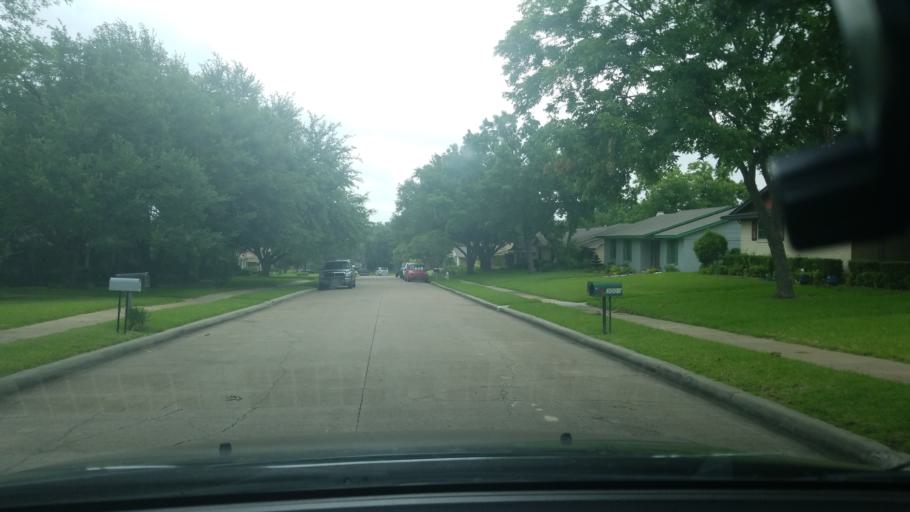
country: US
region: Texas
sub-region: Dallas County
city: Mesquite
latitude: 32.7834
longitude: -96.6422
